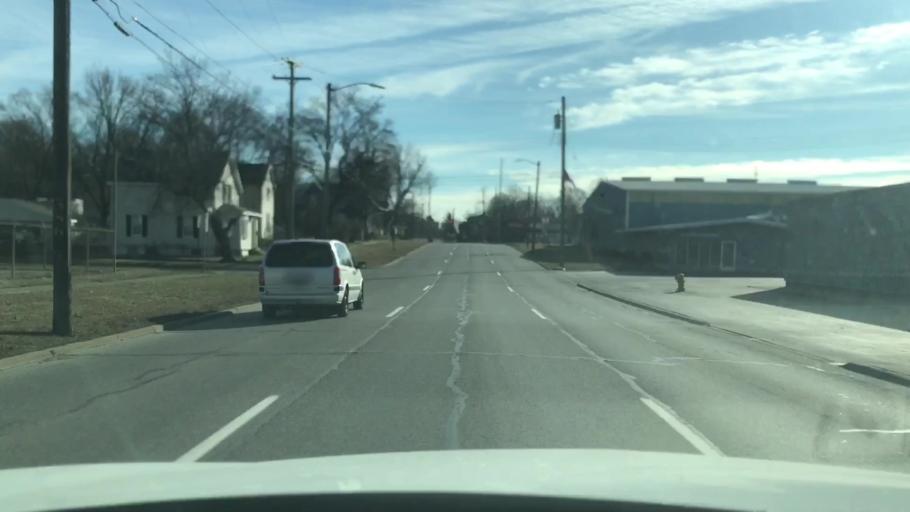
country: US
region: Michigan
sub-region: Oakland County
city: Pontiac
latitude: 42.6460
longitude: -83.3060
